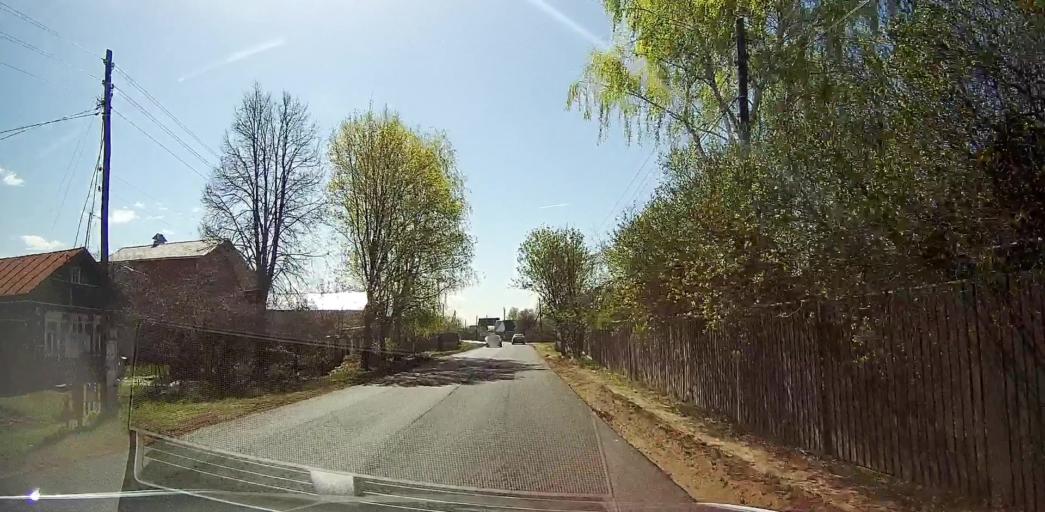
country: RU
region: Moskovskaya
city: Malyshevo
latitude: 55.4770
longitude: 38.3977
